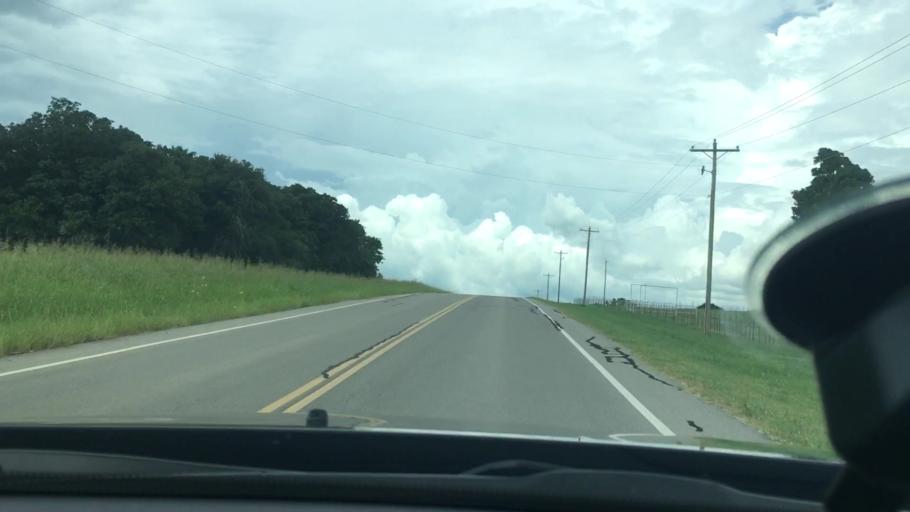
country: US
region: Oklahoma
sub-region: Garvin County
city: Stratford
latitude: 34.8094
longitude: -97.0554
